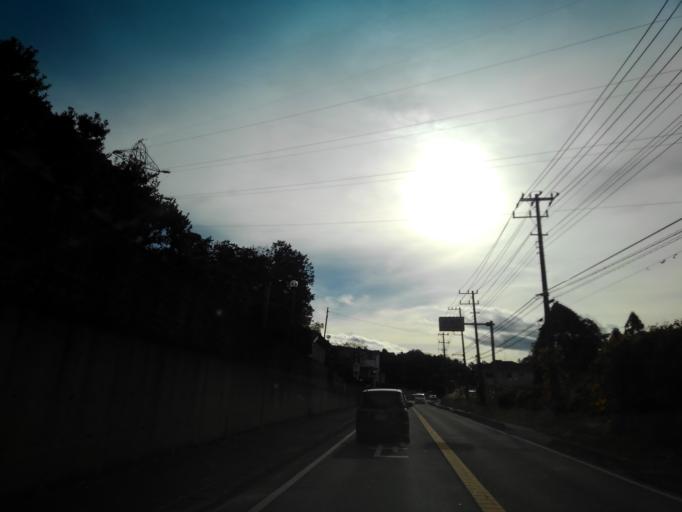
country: JP
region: Saitama
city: Hanno
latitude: 35.8789
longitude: 139.3368
